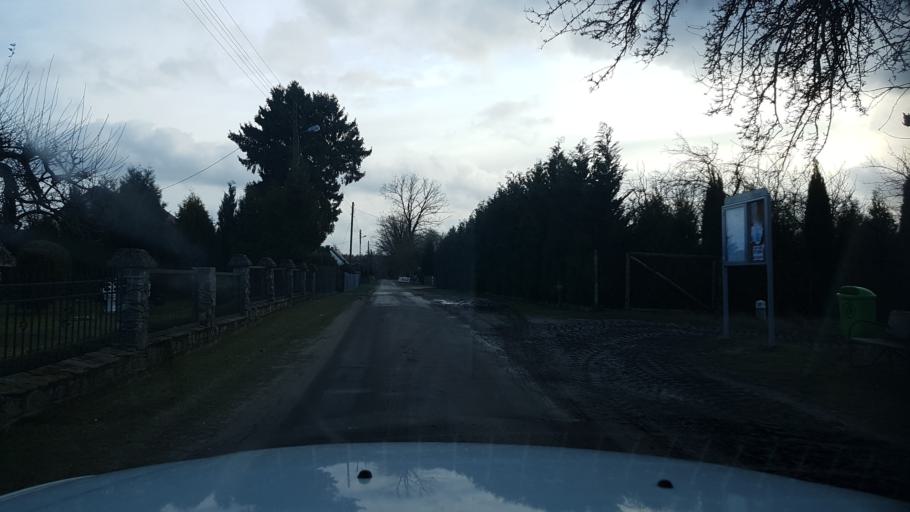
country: PL
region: West Pomeranian Voivodeship
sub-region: Powiat szczecinecki
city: Borne Sulinowo
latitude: 53.6213
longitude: 16.6153
